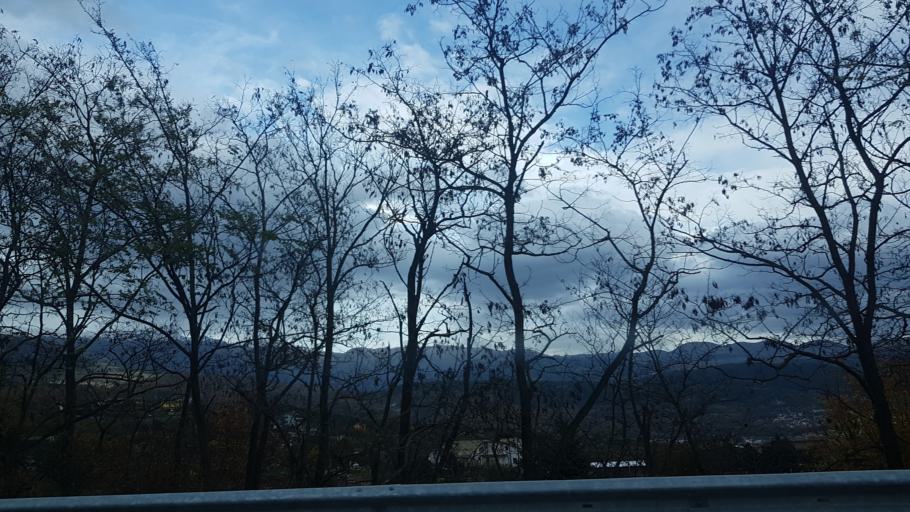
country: IT
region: Abruzzo
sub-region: Provincia dell' Aquila
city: Progetto Case Bazzano
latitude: 42.3635
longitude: 13.4288
